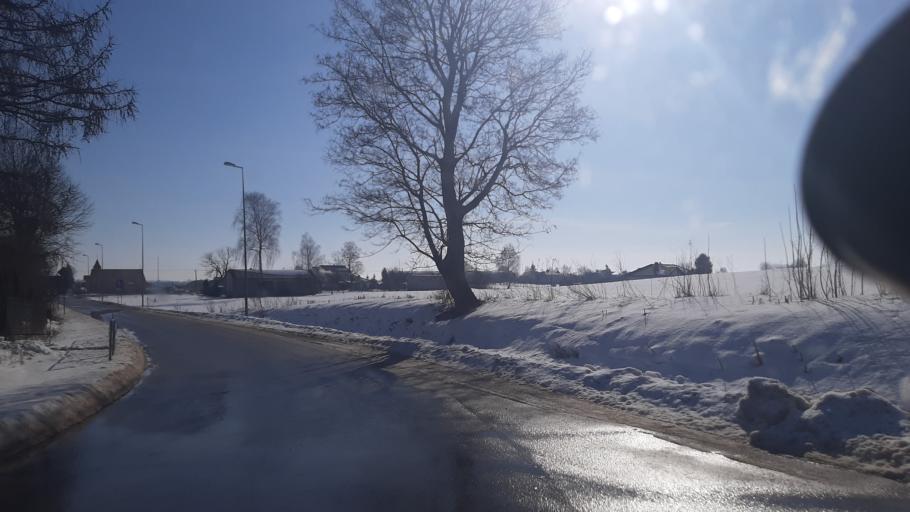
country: PL
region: Lublin Voivodeship
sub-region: Powiat lubelski
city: Garbow
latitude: 51.3055
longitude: 22.3057
